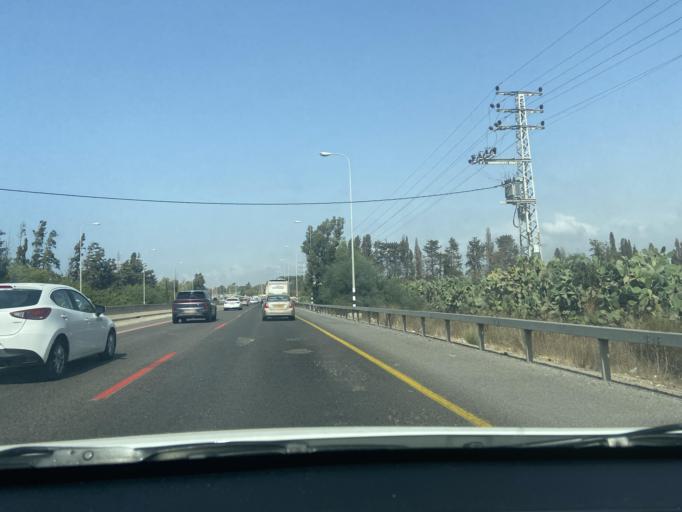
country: IL
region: Northern District
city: El Mazra`a
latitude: 32.9560
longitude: 35.0918
